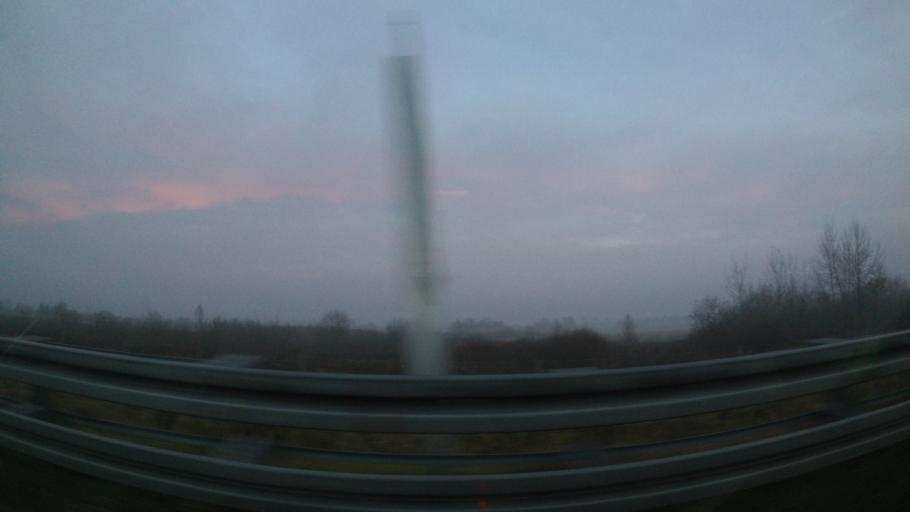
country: HR
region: Zagrebacka
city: Mraclin
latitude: 45.6624
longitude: 16.0756
